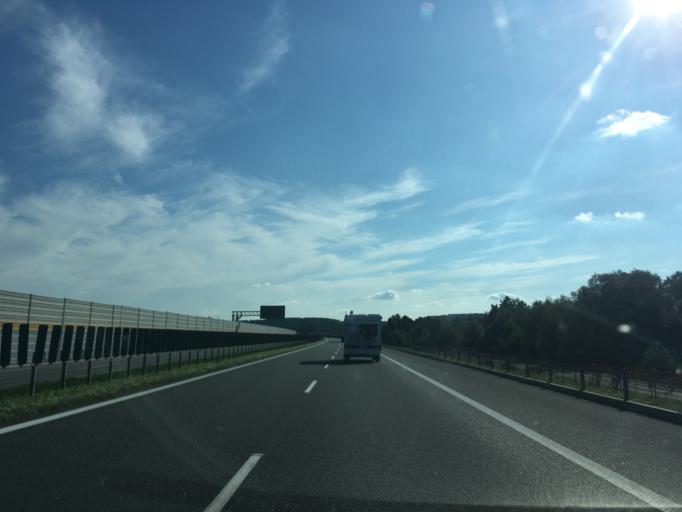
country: PL
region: Kujawsko-Pomorskie
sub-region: Grudziadz
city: Grudziadz
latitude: 53.4110
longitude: 18.6863
